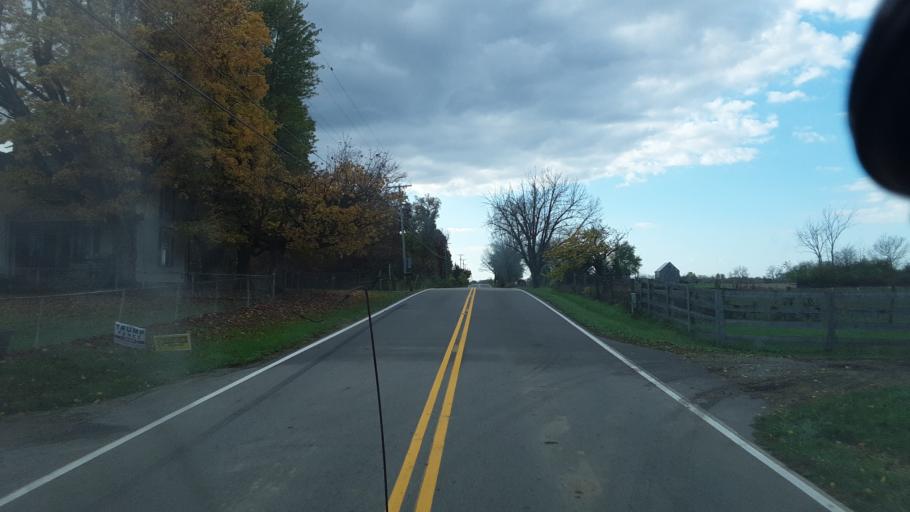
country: US
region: Ohio
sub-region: Highland County
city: Greenfield
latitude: 39.3924
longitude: -83.4661
